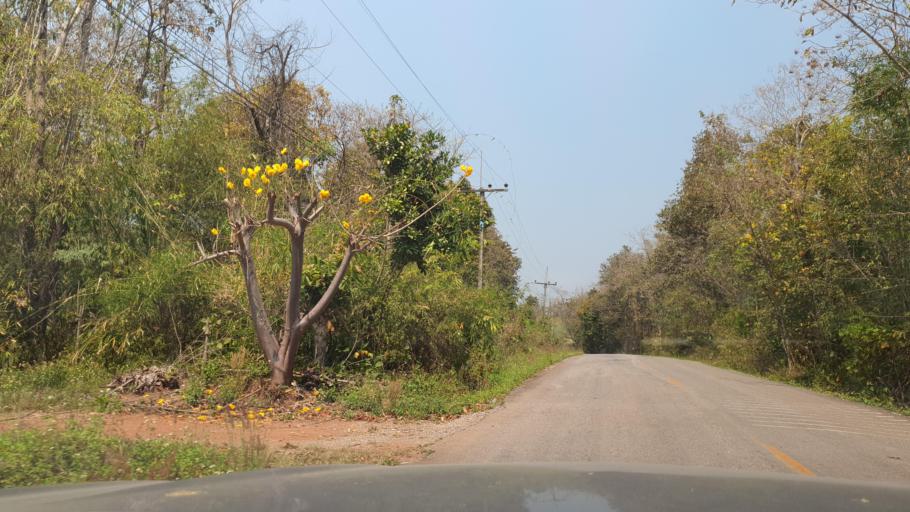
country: TH
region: Chiang Rai
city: Mae Lao
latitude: 19.7346
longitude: 99.6244
